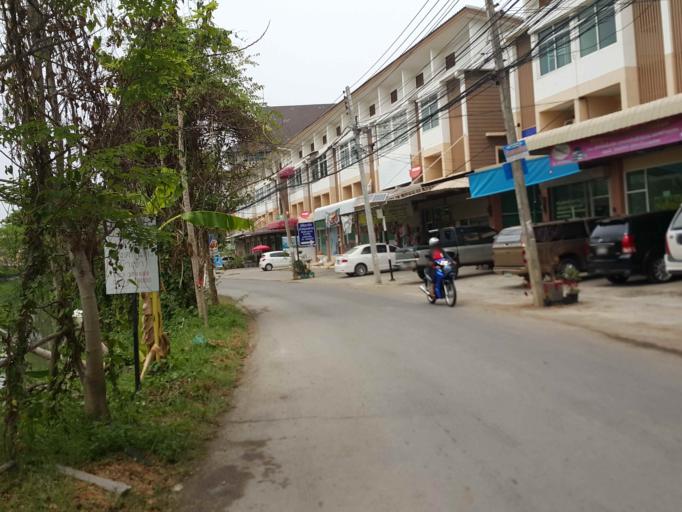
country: TH
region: Chiang Mai
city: Chiang Mai
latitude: 18.7573
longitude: 99.0167
